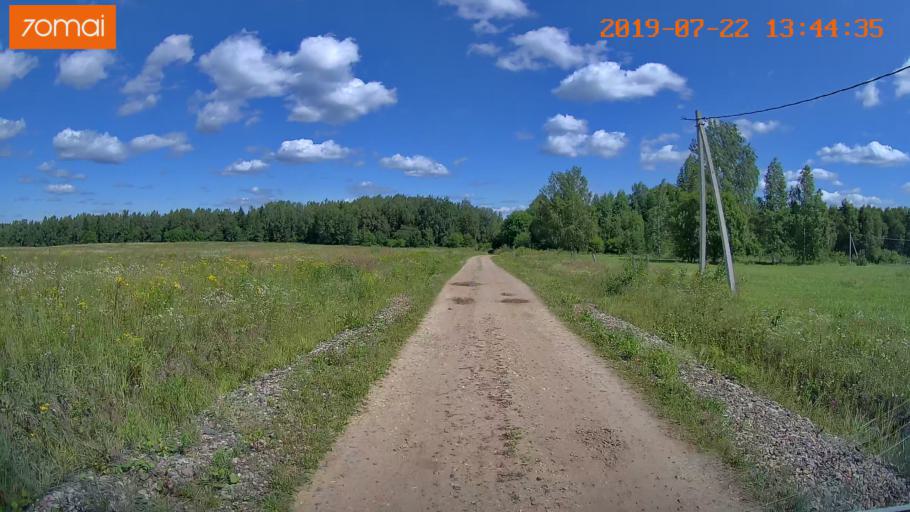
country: RU
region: Ivanovo
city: Novo-Talitsy
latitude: 57.0851
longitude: 40.8769
